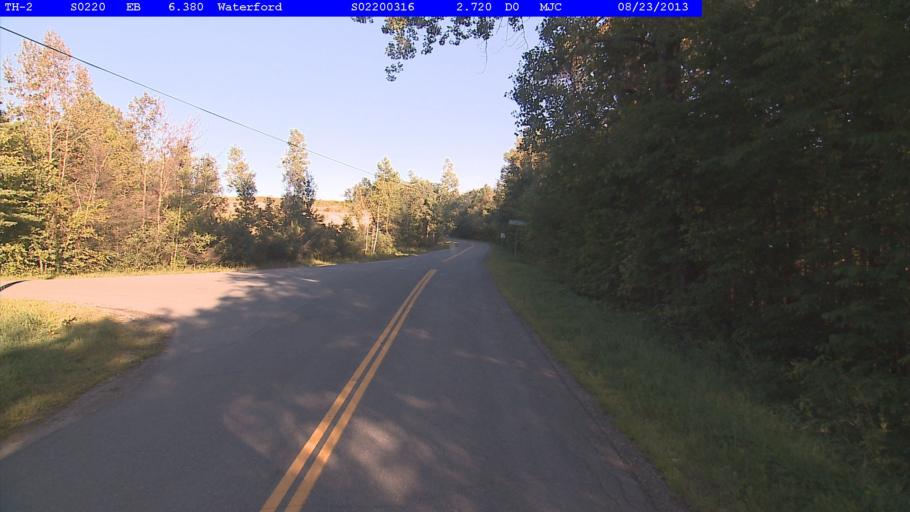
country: US
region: Vermont
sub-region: Caledonia County
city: Saint Johnsbury
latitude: 44.3411
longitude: -71.9489
